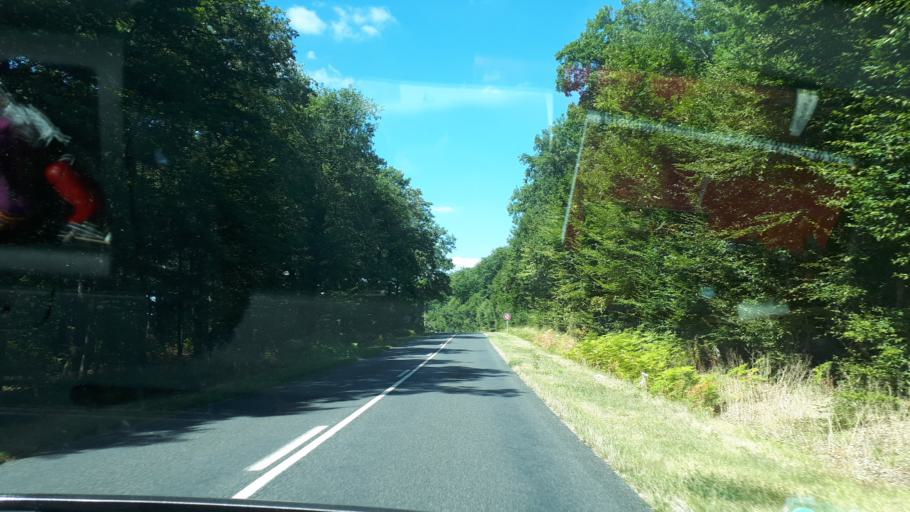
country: FR
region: Centre
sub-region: Departement du Loir-et-Cher
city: Mont-pres-Chambord
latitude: 47.5631
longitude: 1.4803
